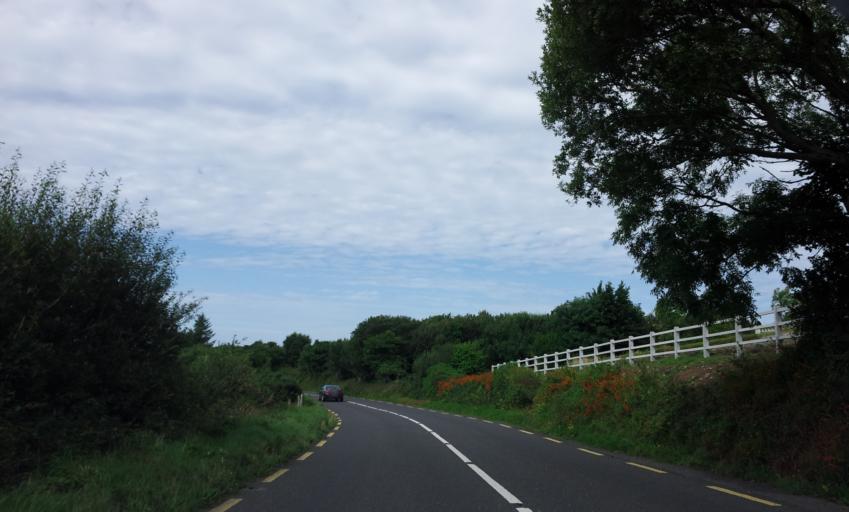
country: IE
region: Munster
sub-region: Ciarrai
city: Killorglin
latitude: 52.0703
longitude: -9.8918
